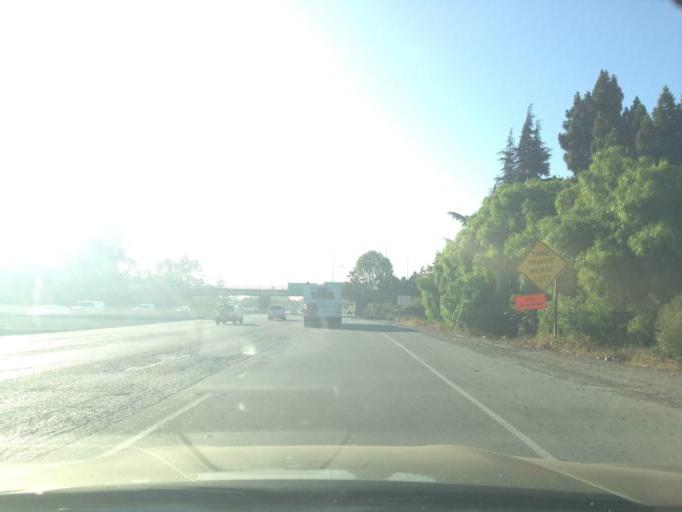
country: US
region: California
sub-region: Santa Clara County
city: Mountain View
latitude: 37.4079
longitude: -122.0684
